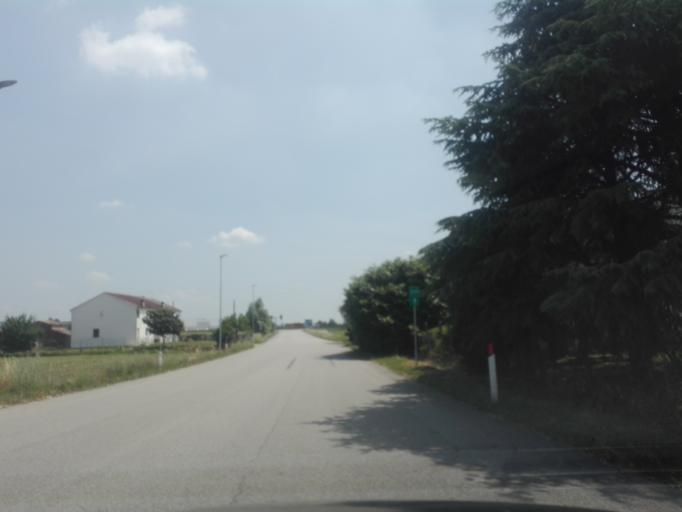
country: IT
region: Veneto
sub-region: Provincia di Rovigo
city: Villamarzana
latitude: 45.0227
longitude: 11.7075
